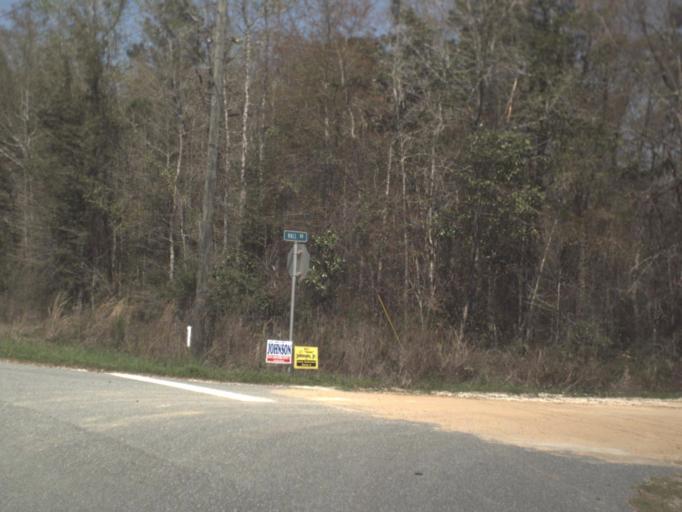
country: US
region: Florida
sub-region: Jackson County
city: Graceville
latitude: 30.9721
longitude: -85.6136
